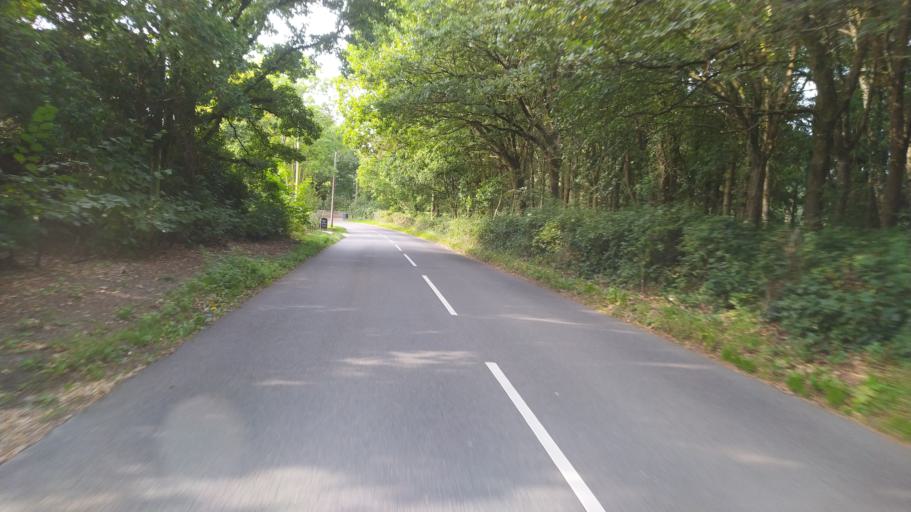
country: GB
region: England
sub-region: Dorset
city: Lytchett Matravers
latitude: 50.7487
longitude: -2.0461
